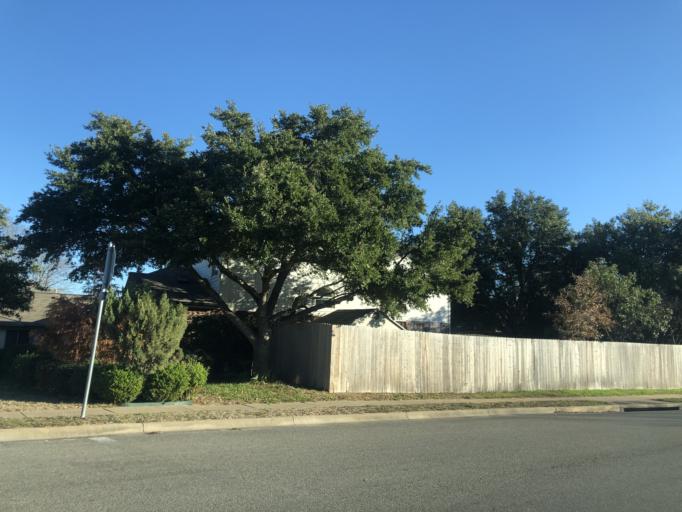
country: US
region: Texas
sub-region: Travis County
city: Windemere
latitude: 30.4815
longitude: -97.6544
